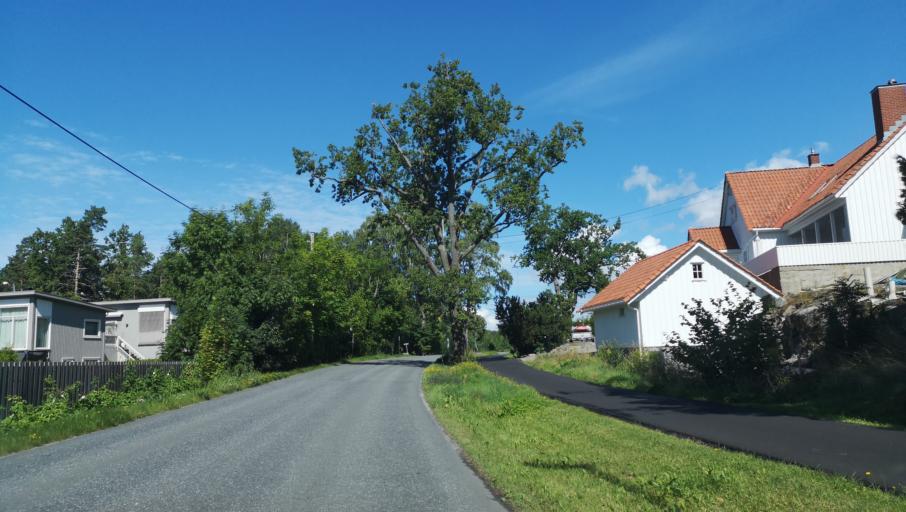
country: NO
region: Akershus
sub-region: Frogn
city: Drobak
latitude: 59.6597
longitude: 10.6395
